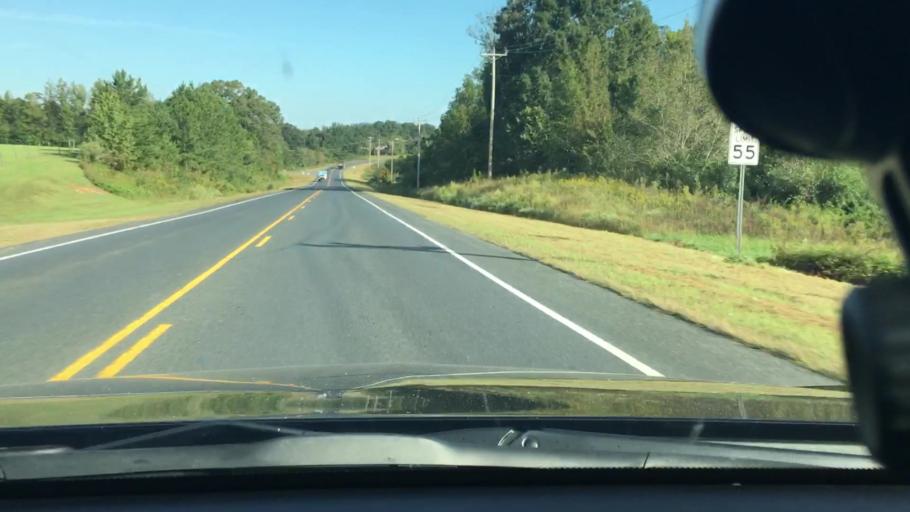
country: US
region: North Carolina
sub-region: Stanly County
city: Albemarle
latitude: 35.3594
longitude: -80.1707
